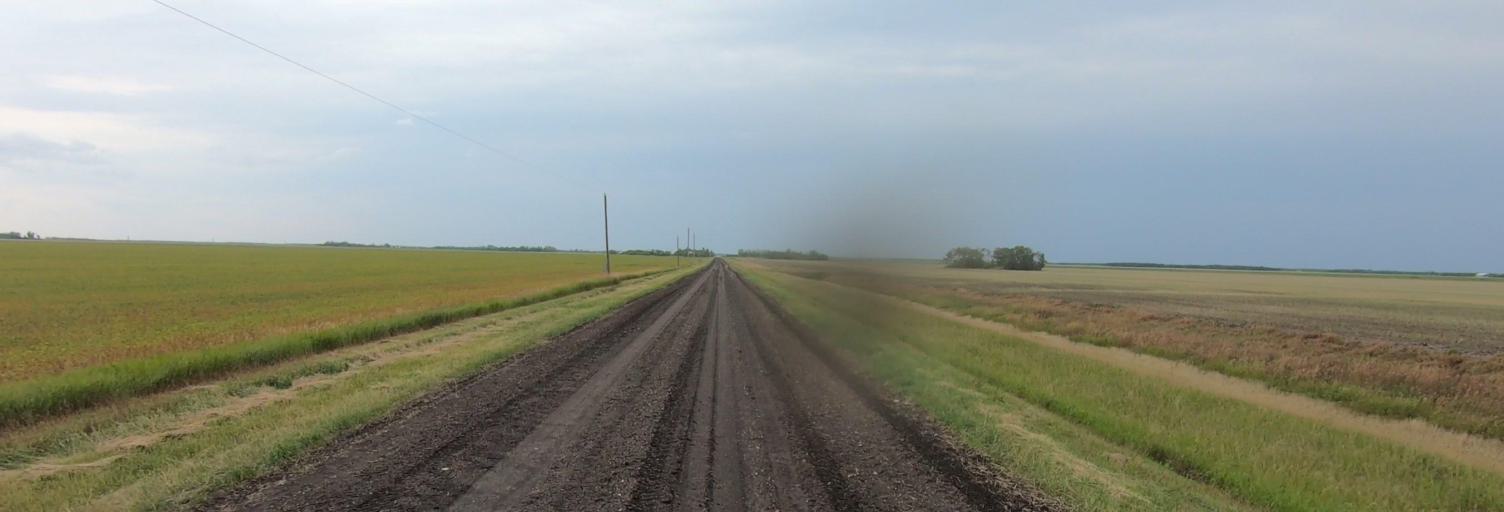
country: CA
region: Manitoba
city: Headingley
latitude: 49.7484
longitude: -97.4135
